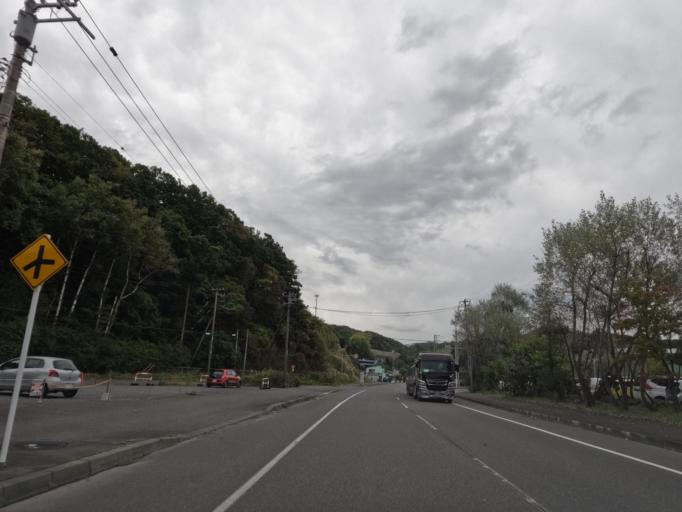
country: JP
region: Hokkaido
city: Muroran
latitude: 42.3736
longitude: 140.9218
